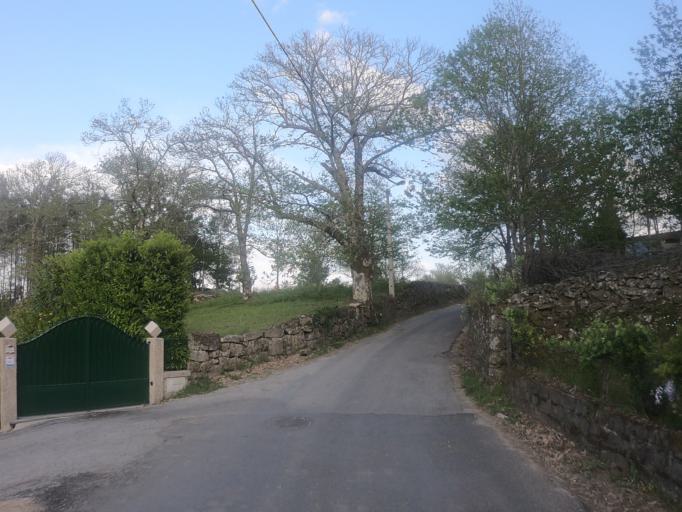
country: PT
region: Vila Real
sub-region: Santa Marta de Penaguiao
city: Santa Marta de Penaguiao
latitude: 41.2768
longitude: -7.8136
